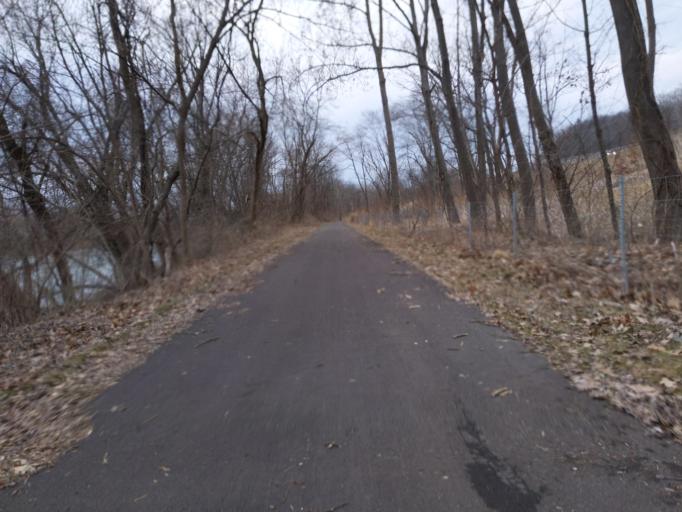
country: US
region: New York
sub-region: Chemung County
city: Southport
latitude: 42.0478
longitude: -76.7478
